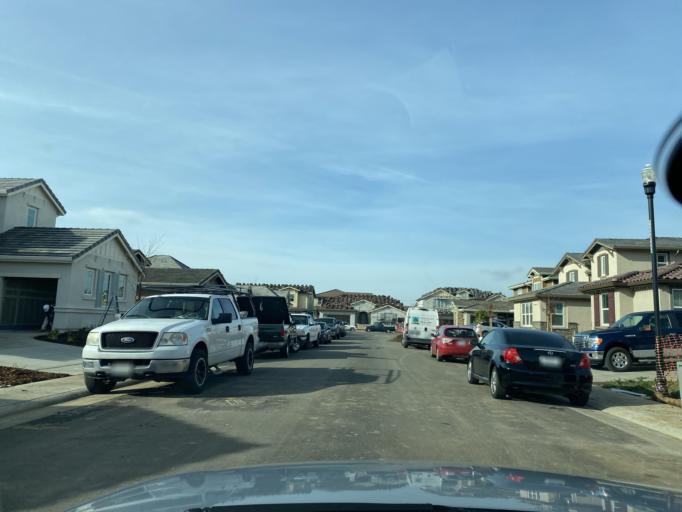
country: US
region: California
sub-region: Sacramento County
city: Elk Grove
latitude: 38.3939
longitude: -121.3840
